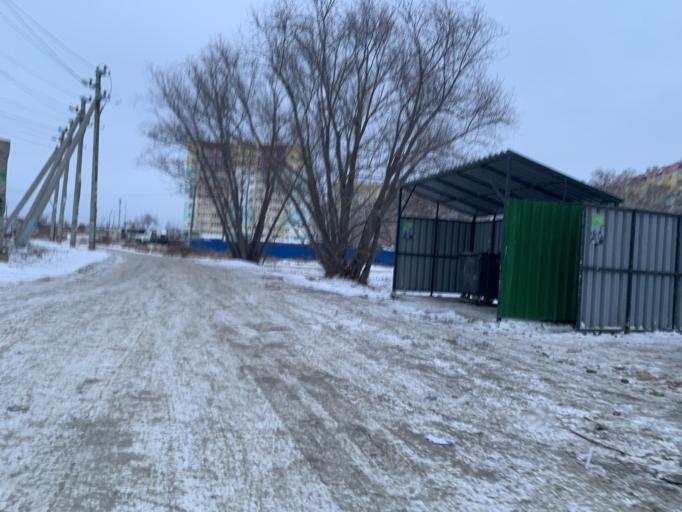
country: RU
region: Chelyabinsk
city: Roshchino
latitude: 55.1880
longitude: 61.2693
